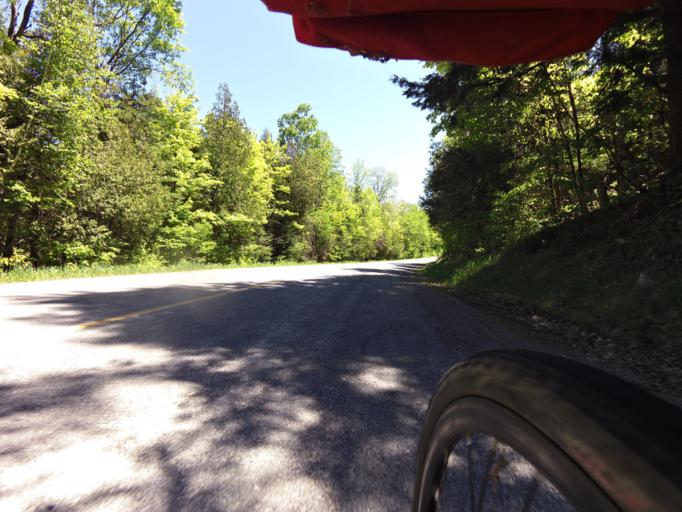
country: CA
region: Ontario
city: Arnprior
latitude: 45.1622
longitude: -76.4417
